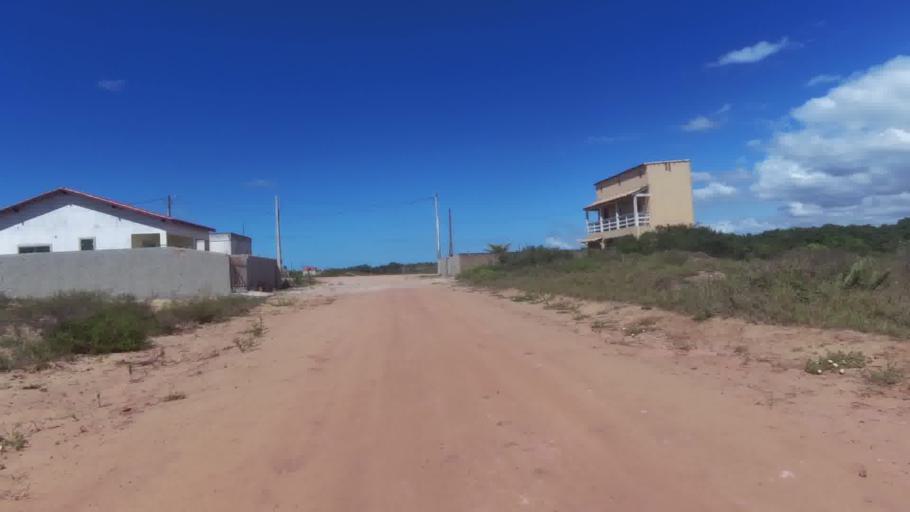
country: BR
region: Espirito Santo
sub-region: Marataizes
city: Marataizes
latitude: -21.2778
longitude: -40.9663
